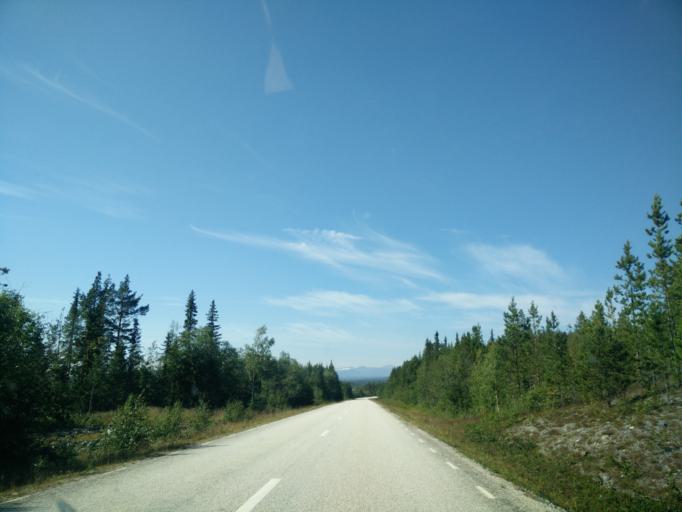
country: SE
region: Jaemtland
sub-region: Are Kommun
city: Jarpen
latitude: 62.8080
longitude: 13.5340
